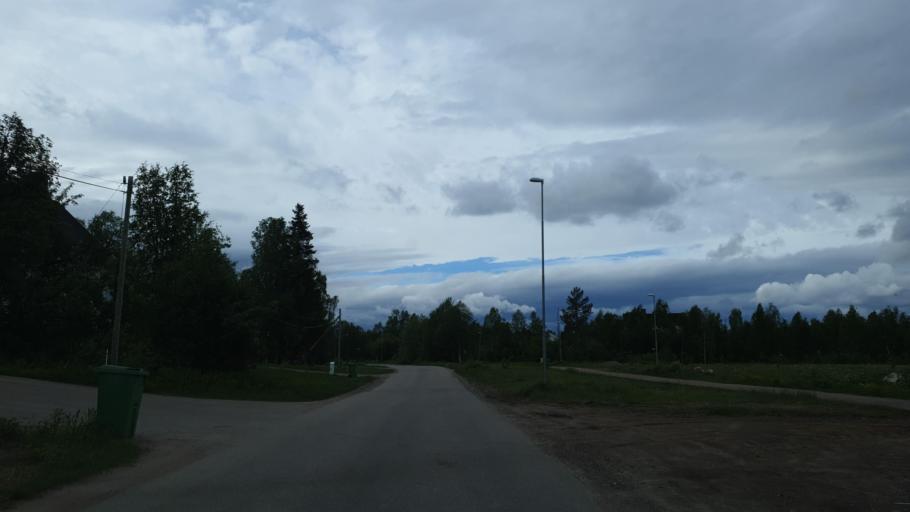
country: SE
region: Norrbotten
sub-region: Gallivare Kommun
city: Gaellivare
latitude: 67.1301
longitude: 20.6464
